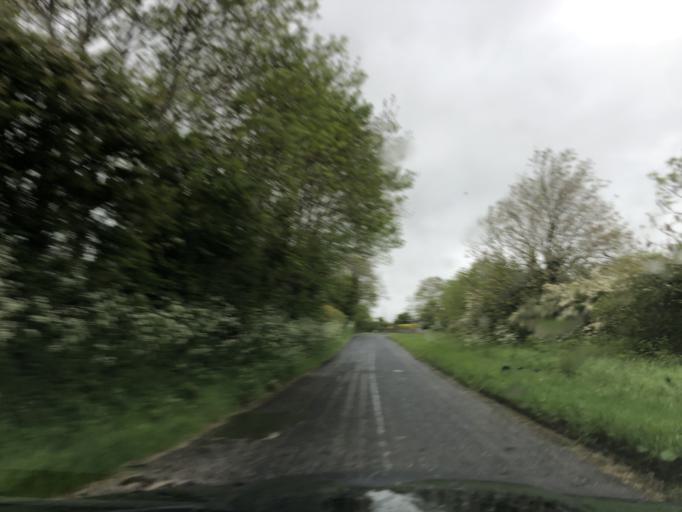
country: GB
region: Northern Ireland
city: Dunloy
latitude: 55.1156
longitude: -6.3510
